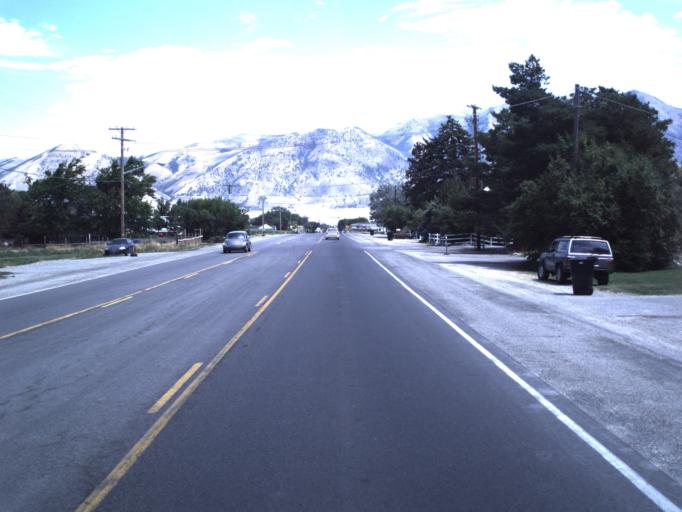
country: US
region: Utah
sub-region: Box Elder County
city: Tremonton
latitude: 41.7121
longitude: -112.1503
